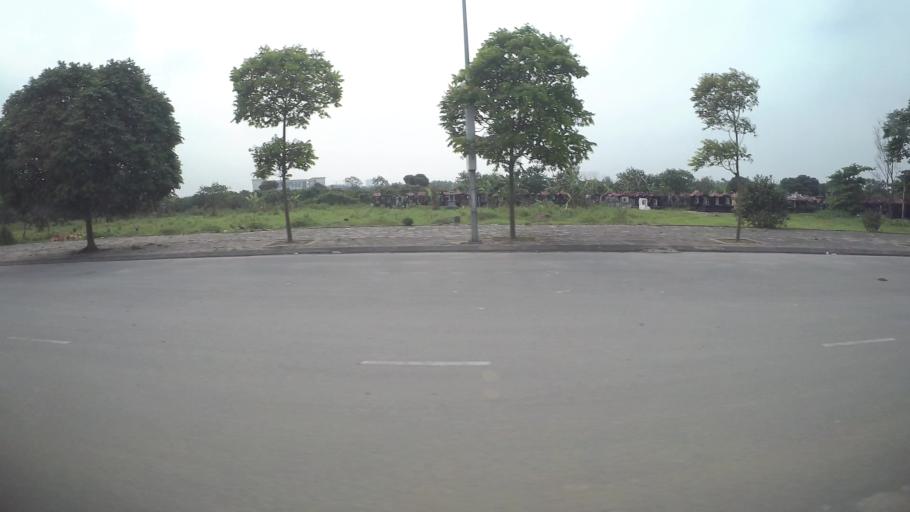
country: VN
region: Ha Noi
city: Hoan Kiem
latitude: 21.0740
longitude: 105.8969
